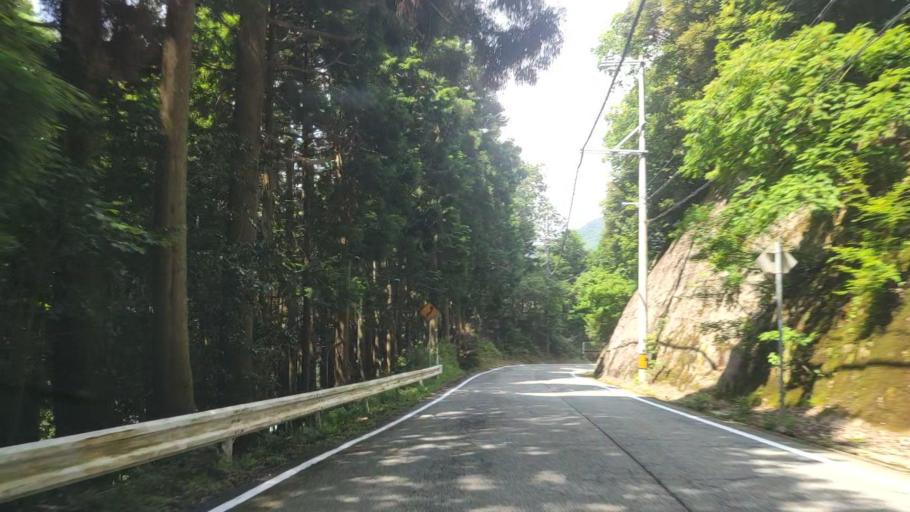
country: JP
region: Hyogo
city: Toyooka
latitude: 35.6418
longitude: 134.7656
